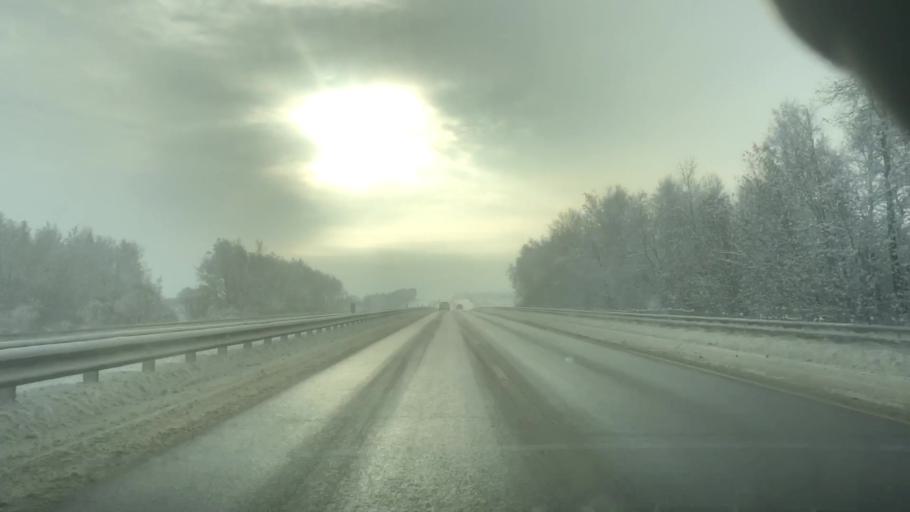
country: RU
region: Tula
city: Venev
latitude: 54.3258
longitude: 38.1545
